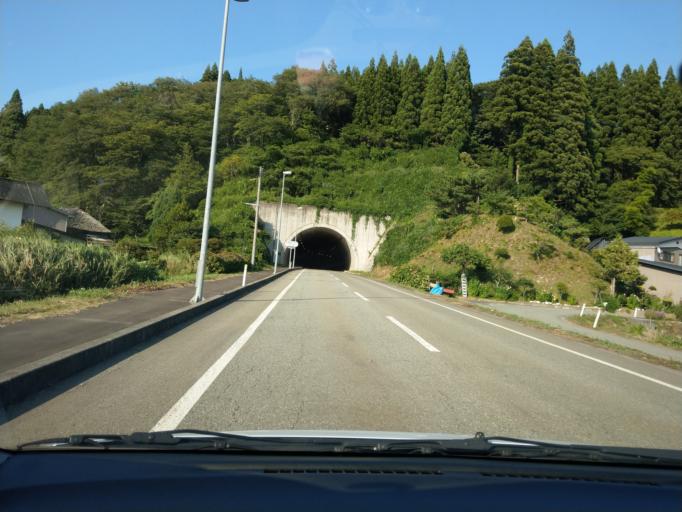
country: JP
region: Akita
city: Akita
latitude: 39.6022
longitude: 140.2188
